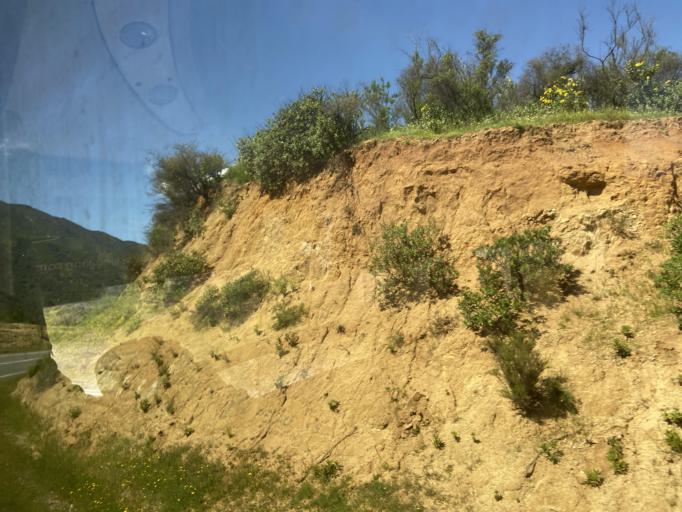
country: CL
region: Valparaiso
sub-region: Provincia de Marga Marga
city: Villa Alemana
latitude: -33.1892
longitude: -71.2917
